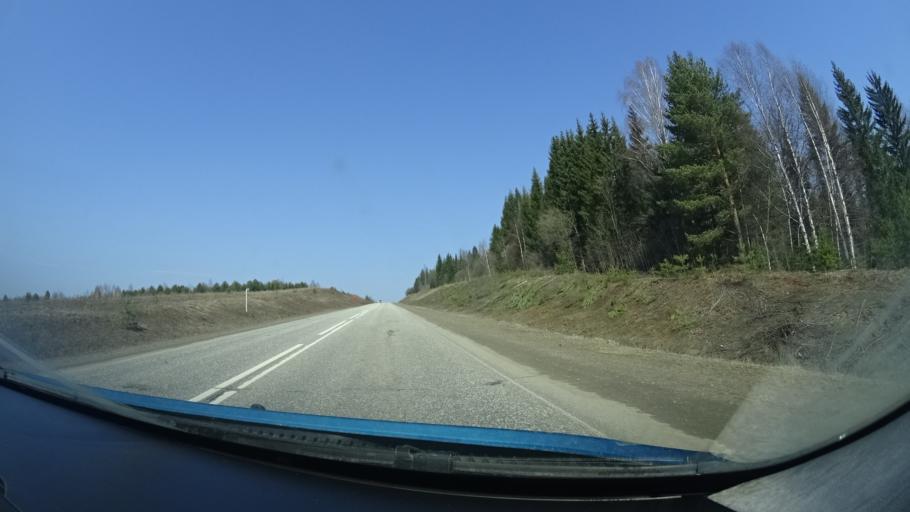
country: RU
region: Perm
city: Osa
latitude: 57.4231
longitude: 55.6225
